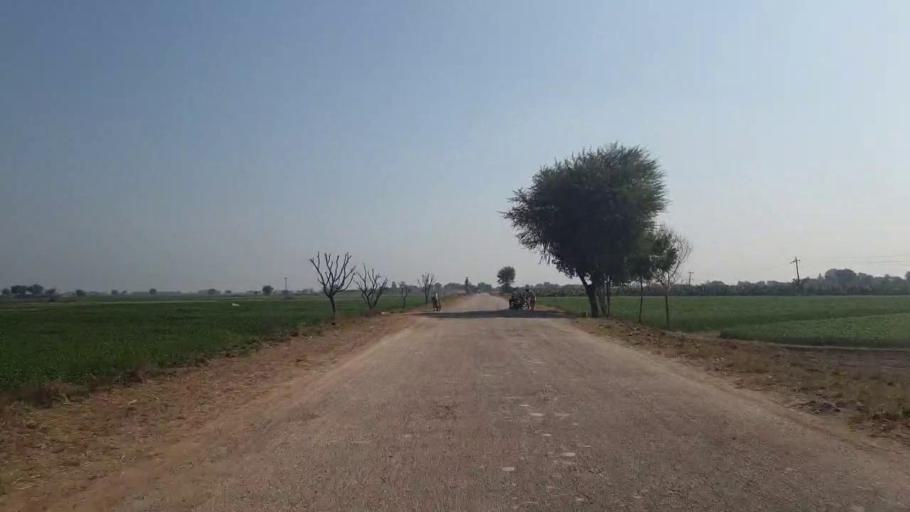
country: PK
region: Sindh
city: Sakrand
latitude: 26.0420
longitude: 68.4268
